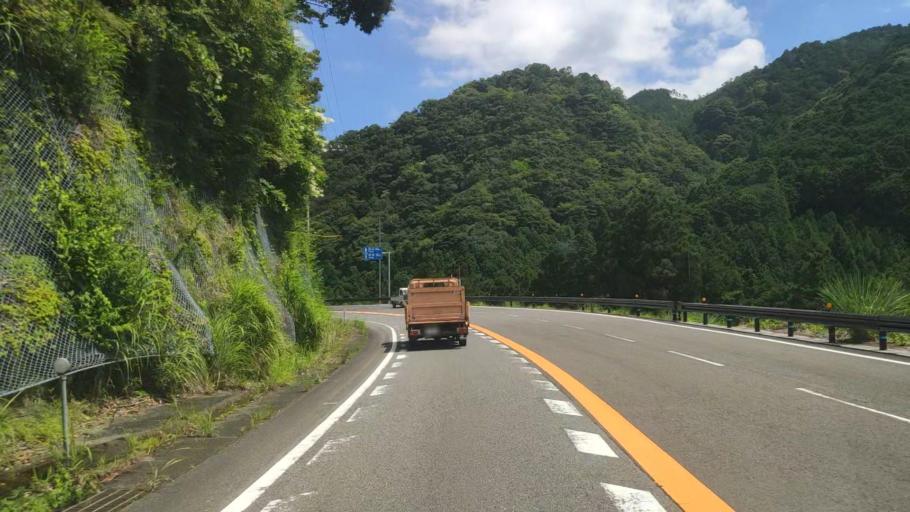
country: JP
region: Mie
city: Owase
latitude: 33.9221
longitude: 136.0963
